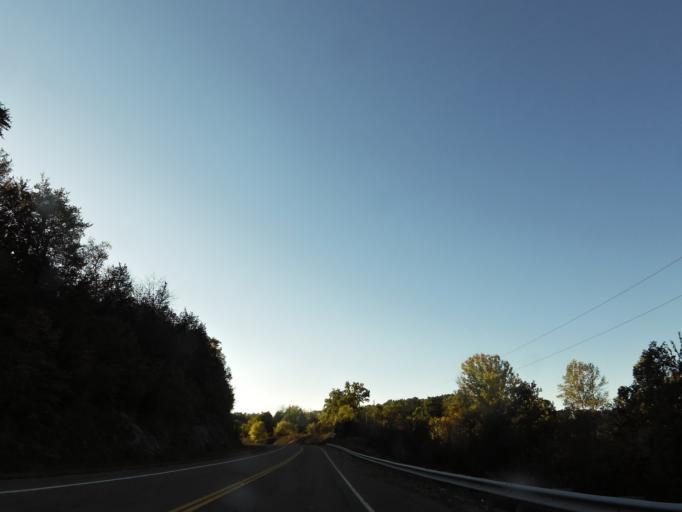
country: US
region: Tennessee
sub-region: Grainger County
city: Rutledge
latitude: 36.3546
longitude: -83.4298
